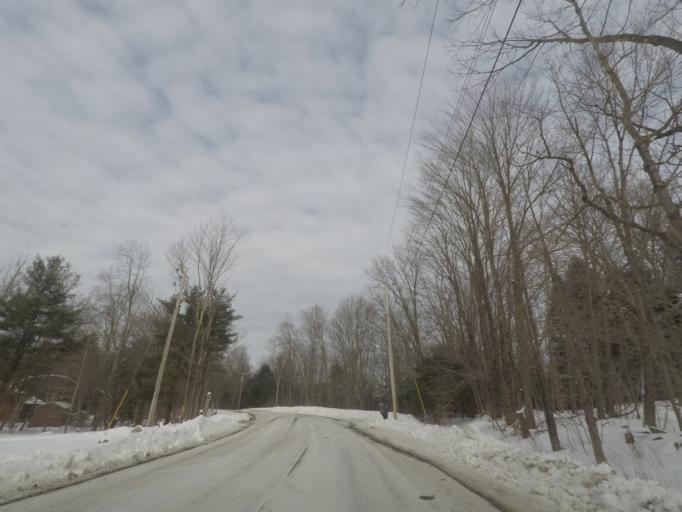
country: US
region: New York
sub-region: Rensselaer County
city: Averill Park
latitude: 42.5995
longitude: -73.4813
